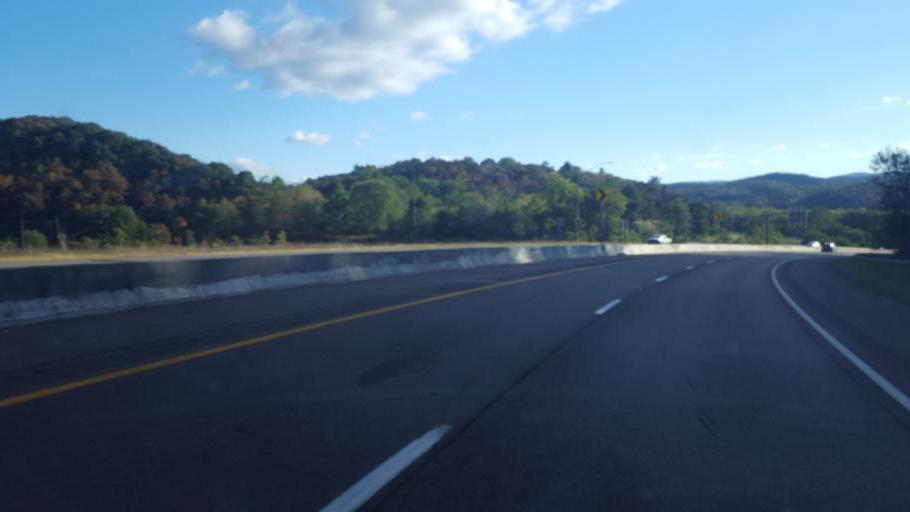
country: US
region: Maryland
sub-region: Allegany County
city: Cumberland
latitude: 39.6728
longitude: -78.7307
